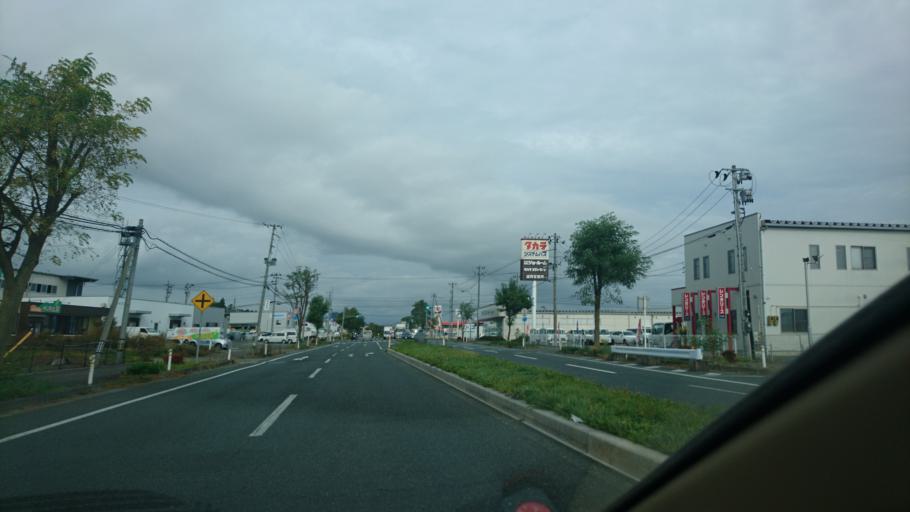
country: JP
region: Iwate
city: Morioka-shi
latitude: 39.6288
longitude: 141.1183
